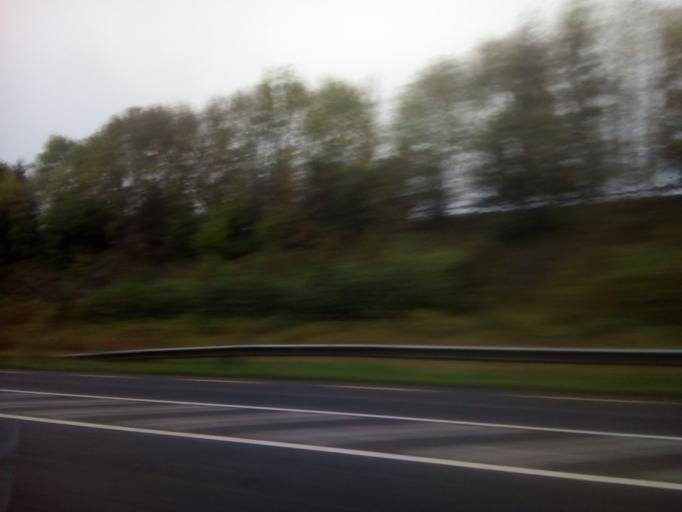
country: IE
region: Leinster
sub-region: An Iarmhi
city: An Muileann gCearr
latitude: 53.5571
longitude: -7.3475
